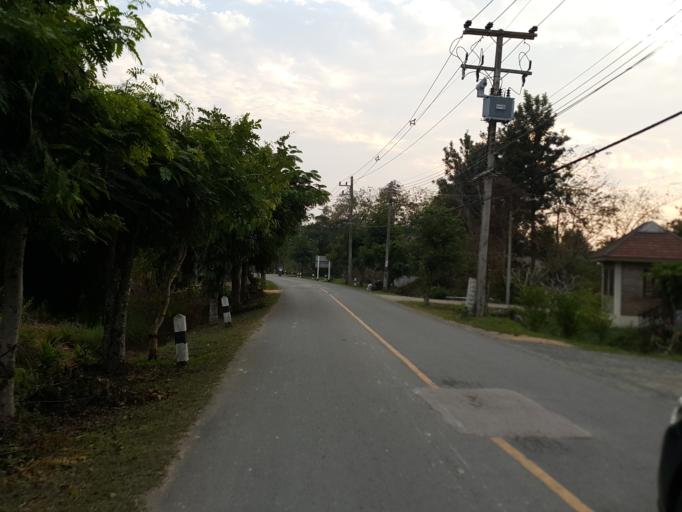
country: TH
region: Chiang Mai
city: San Sai
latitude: 18.8884
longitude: 99.1243
